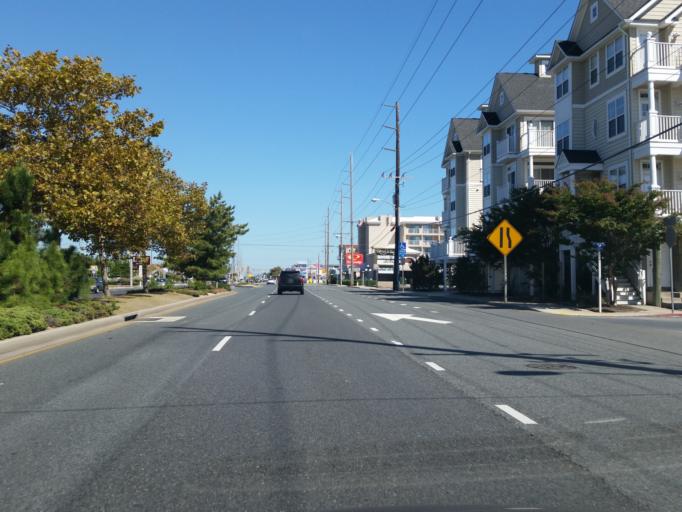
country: US
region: Delaware
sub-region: Sussex County
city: Bethany Beach
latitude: 38.4492
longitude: -75.0524
